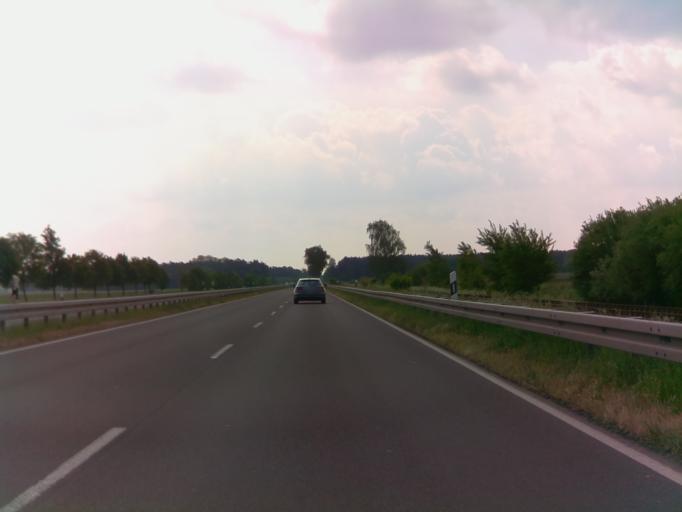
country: DE
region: Saxony-Anhalt
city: Stendal
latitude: 52.5761
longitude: 11.9139
